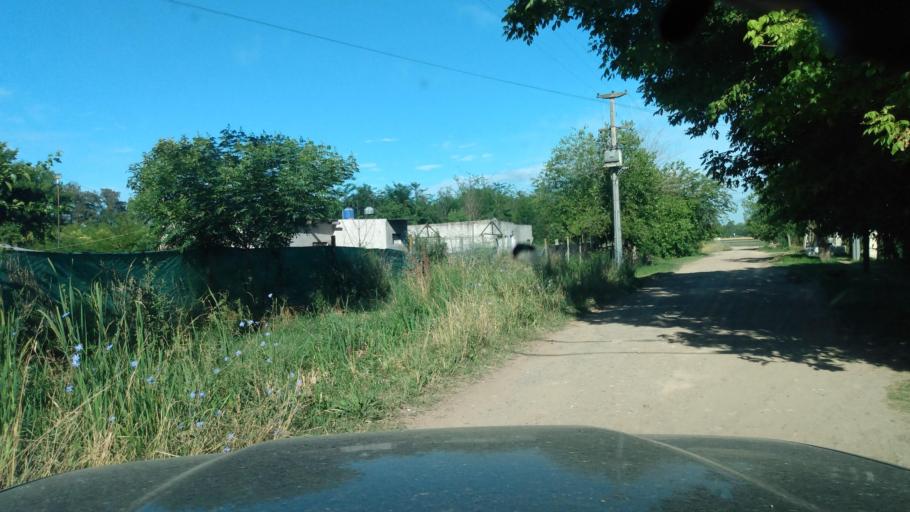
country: AR
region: Buenos Aires
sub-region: Partido de Lujan
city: Lujan
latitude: -34.5890
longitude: -59.0599
